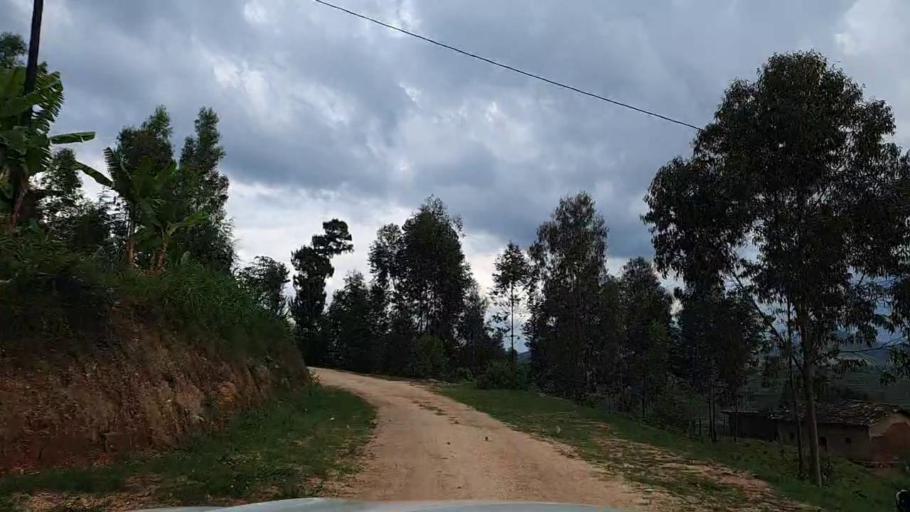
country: RW
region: Southern Province
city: Gikongoro
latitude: -2.4362
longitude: 29.6349
